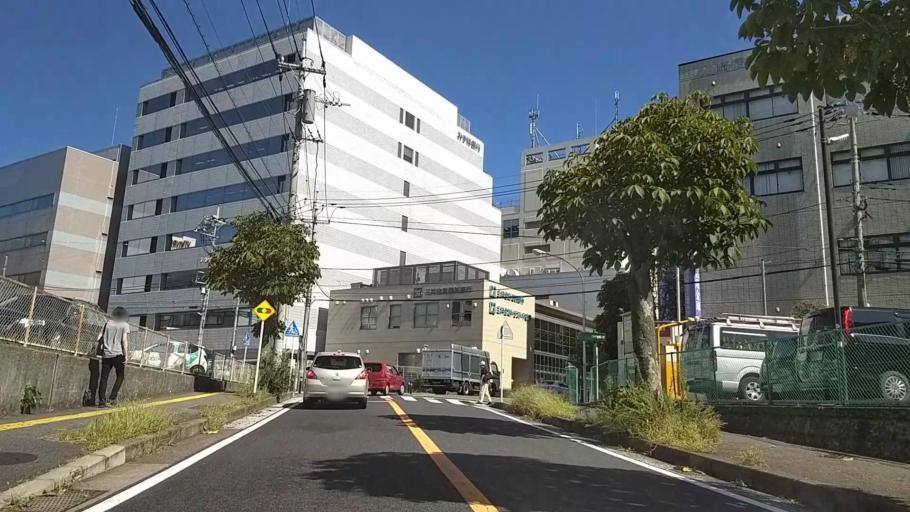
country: JP
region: Tokyo
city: Chofugaoka
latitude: 35.6018
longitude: 139.5088
